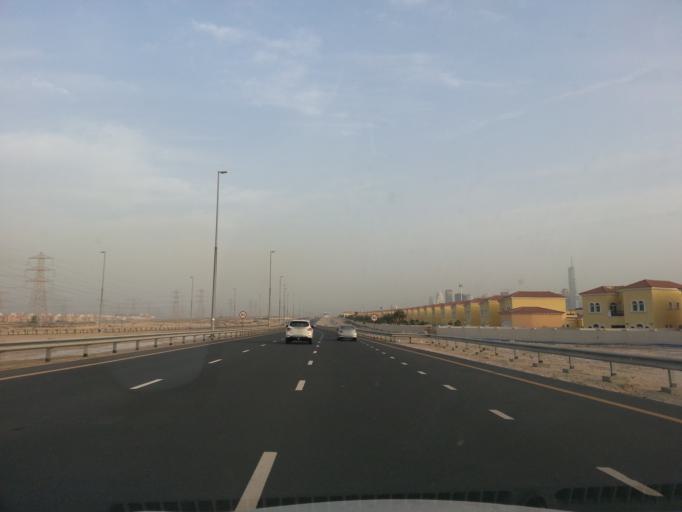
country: AE
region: Dubai
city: Dubai
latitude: 25.0420
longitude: 55.1550
